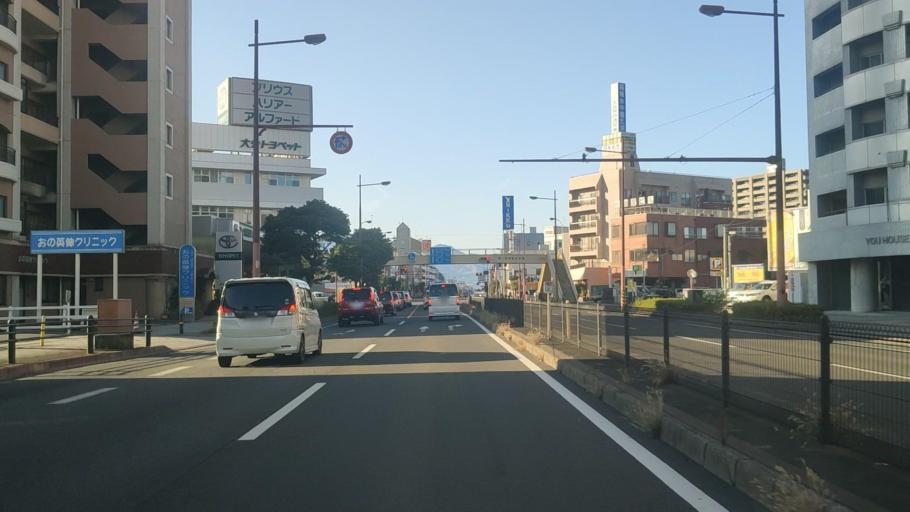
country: JP
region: Oita
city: Oita
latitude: 33.2414
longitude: 131.5929
